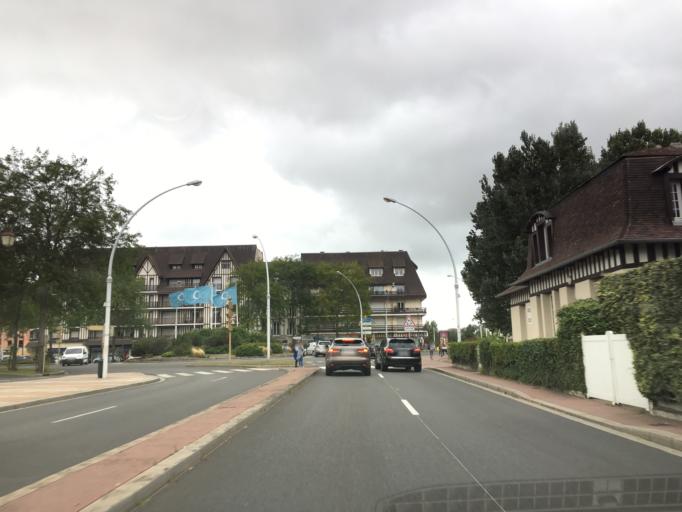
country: FR
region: Lower Normandy
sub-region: Departement du Calvados
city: Trouville-sur-Mer
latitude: 49.3601
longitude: 0.0850
